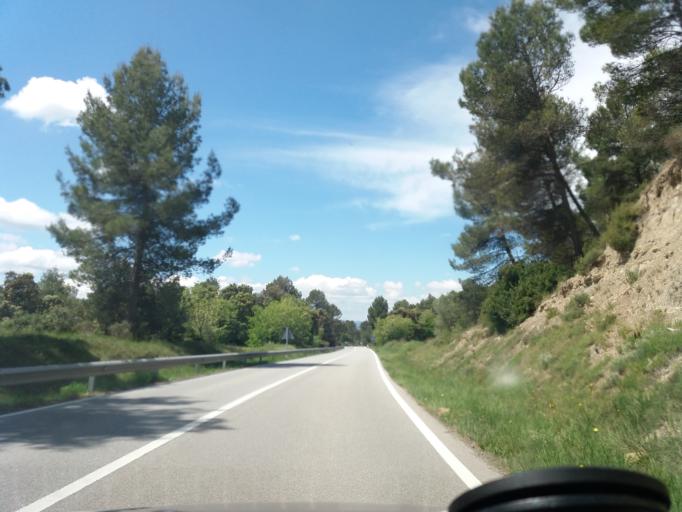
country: ES
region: Catalonia
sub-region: Provincia de Barcelona
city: Artes
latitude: 41.7736
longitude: 1.9620
